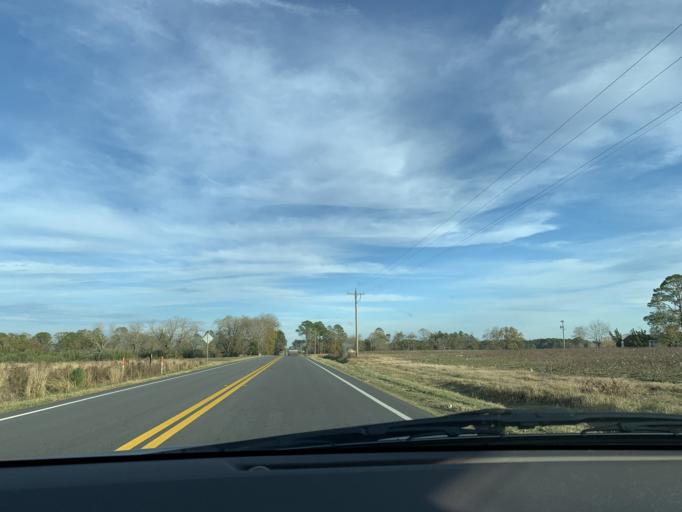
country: US
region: Georgia
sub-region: Irwin County
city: Ocilla
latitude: 31.5925
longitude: -83.2333
